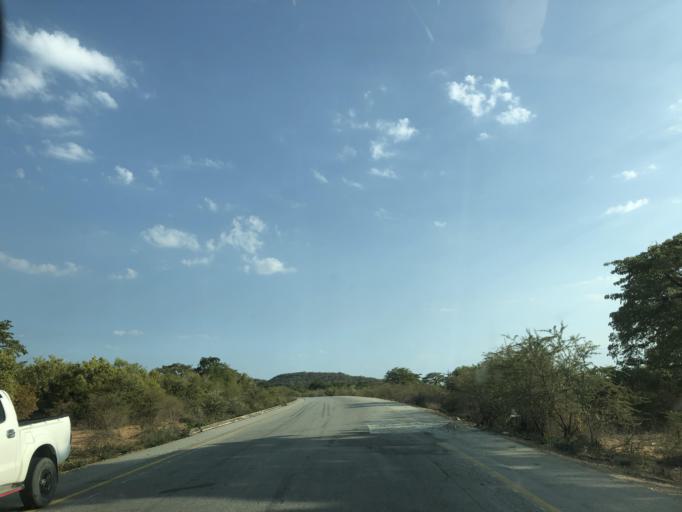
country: AO
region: Benguela
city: Benguela
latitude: -13.2408
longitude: 13.7721
